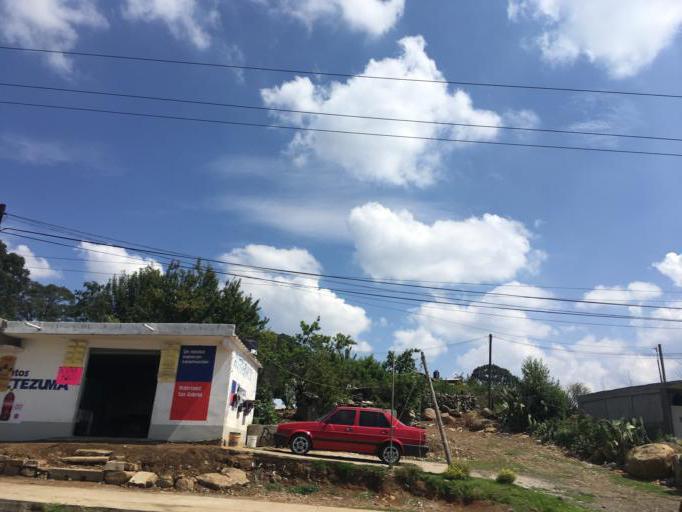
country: MX
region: Mexico
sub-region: Jilotepec
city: Doxhicho
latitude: 19.8924
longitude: -99.6271
